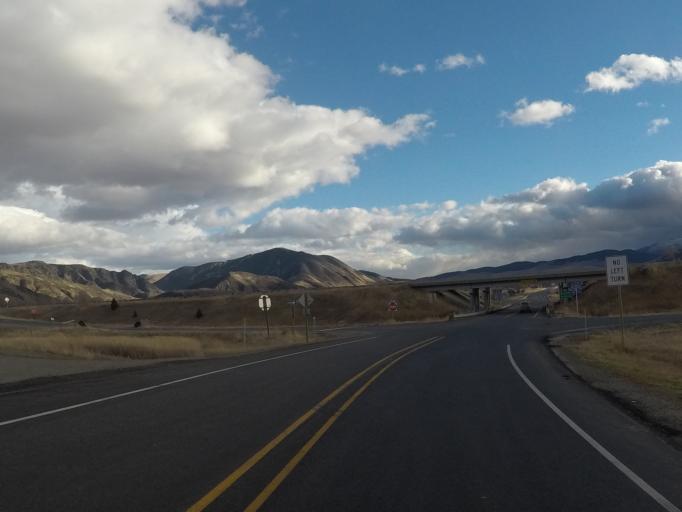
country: US
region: Montana
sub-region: Jefferson County
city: Whitehall
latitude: 45.8709
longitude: -111.9549
